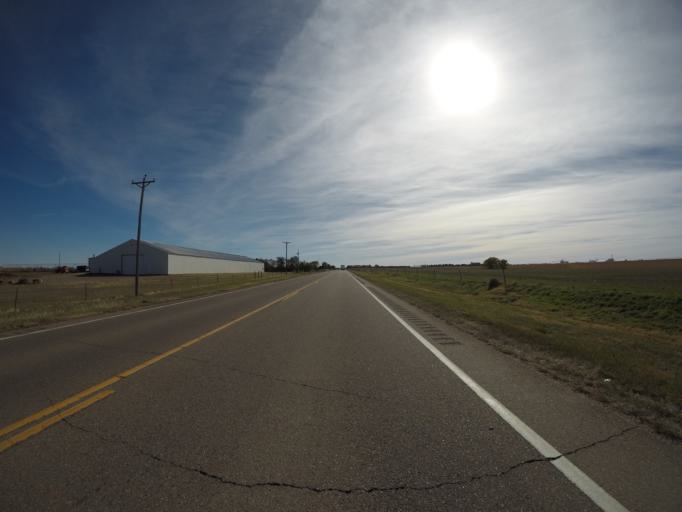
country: US
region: Colorado
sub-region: Kit Carson County
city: Burlington
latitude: 39.3293
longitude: -102.2600
